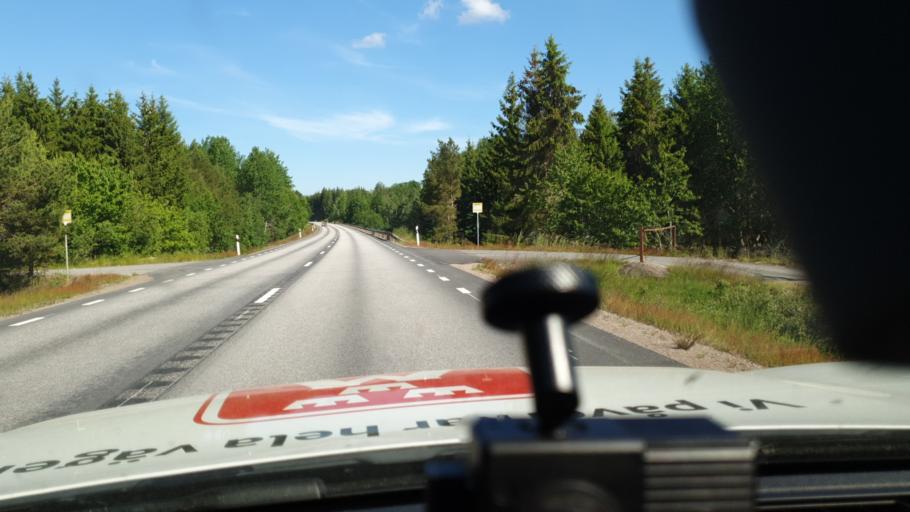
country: SE
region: Kalmar
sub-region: Vasterviks Kommun
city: Ankarsrum
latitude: 57.7106
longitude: 16.1210
